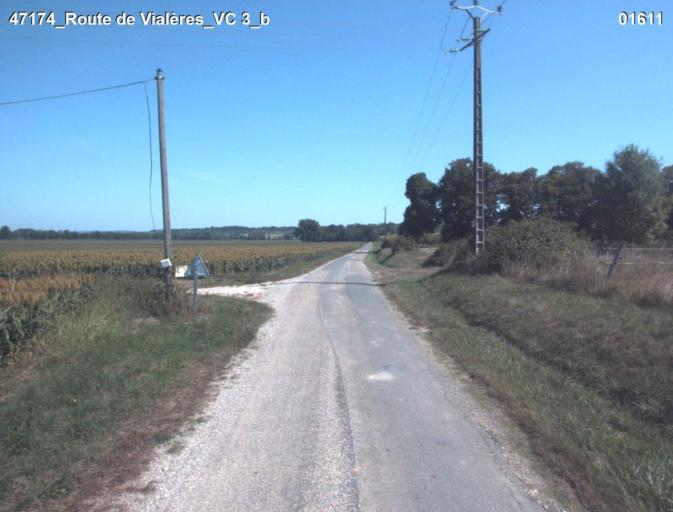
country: FR
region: Midi-Pyrenees
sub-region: Departement du Gers
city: Condom
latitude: 44.0476
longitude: 0.3803
